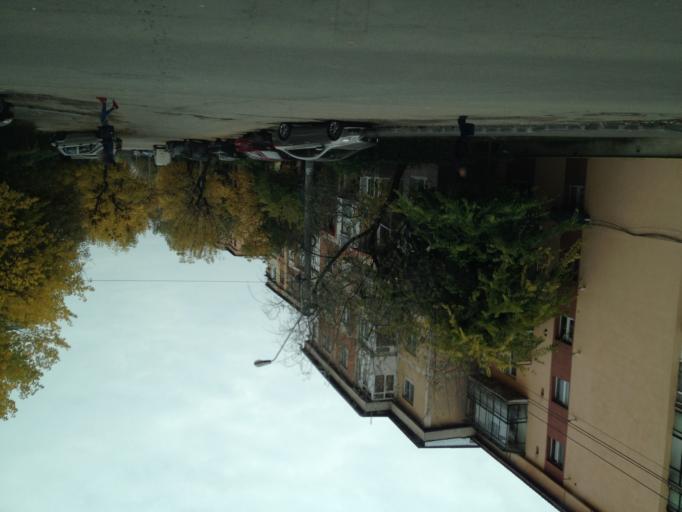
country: RO
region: Dolj
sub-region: Municipiul Craiova
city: Popoveni
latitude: 44.2991
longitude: 23.7943
